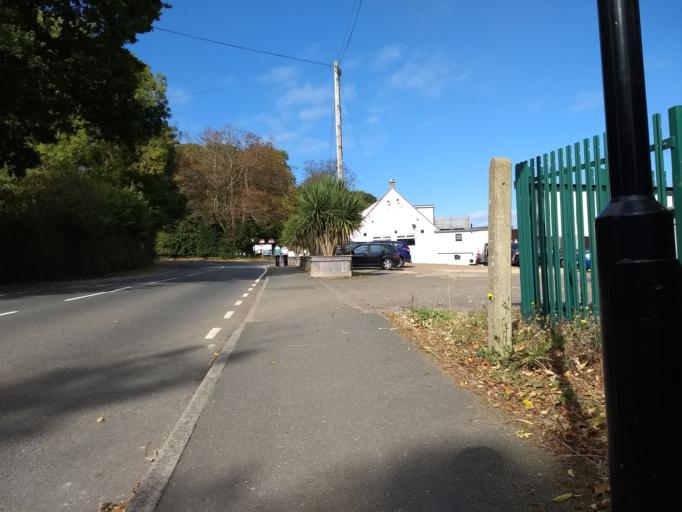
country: GB
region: England
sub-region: Isle of Wight
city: Seaview
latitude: 50.7161
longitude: -1.1244
